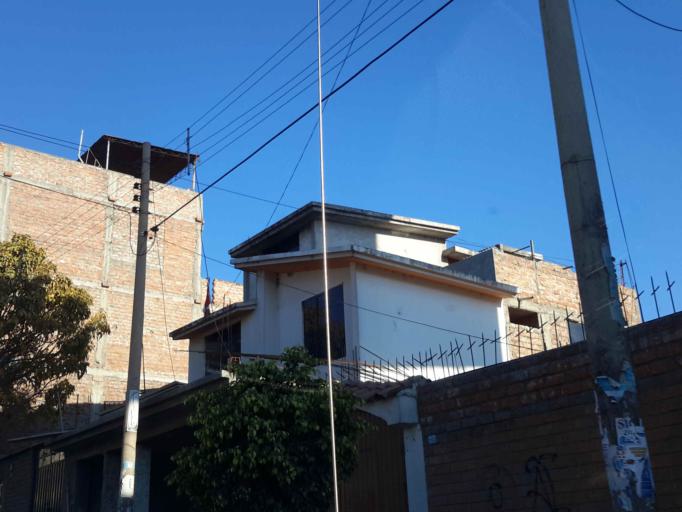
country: PE
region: Ayacucho
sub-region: Provincia de Huamanga
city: Ayacucho
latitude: -13.1435
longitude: -74.2277
